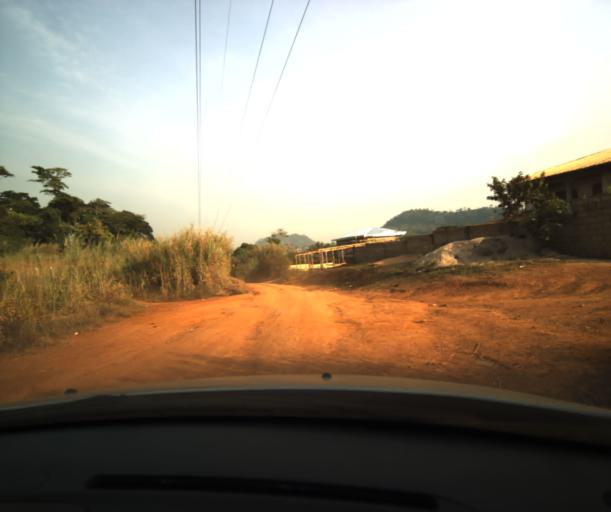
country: CM
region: Centre
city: Yaounde
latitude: 3.8759
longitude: 11.4285
